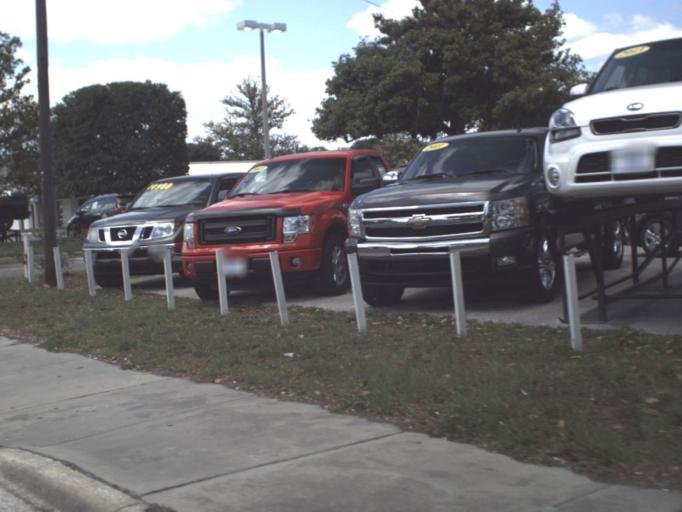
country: US
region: Florida
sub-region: Marion County
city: Ocala
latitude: 29.1744
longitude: -82.1585
